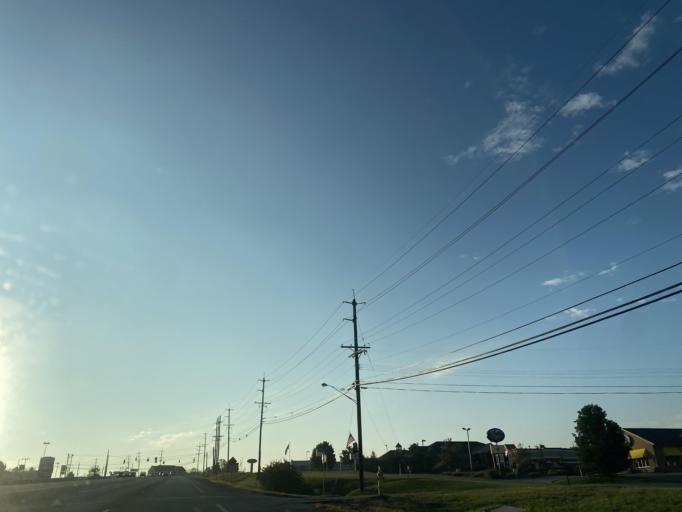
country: US
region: Kentucky
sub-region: Campbell County
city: Alexandria
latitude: 38.9845
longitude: -84.4015
